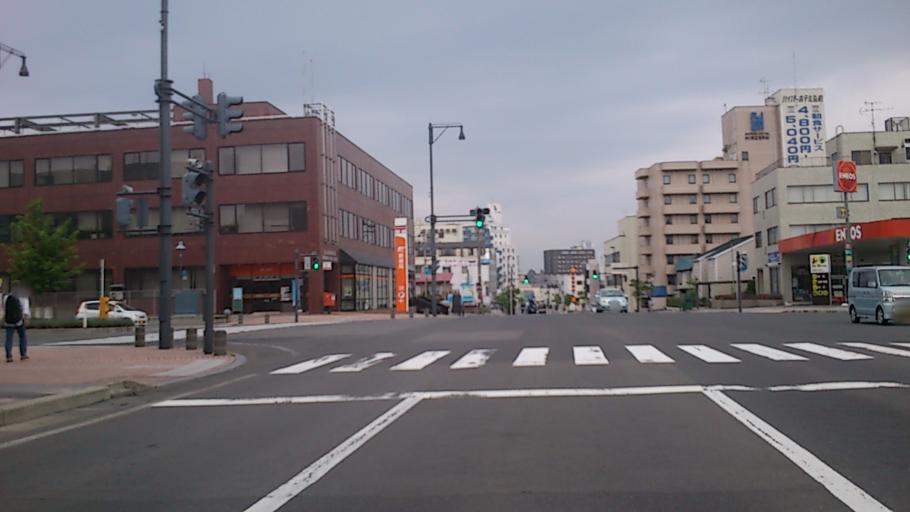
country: JP
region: Aomori
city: Hirosaki
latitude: 40.6013
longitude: 140.4772
